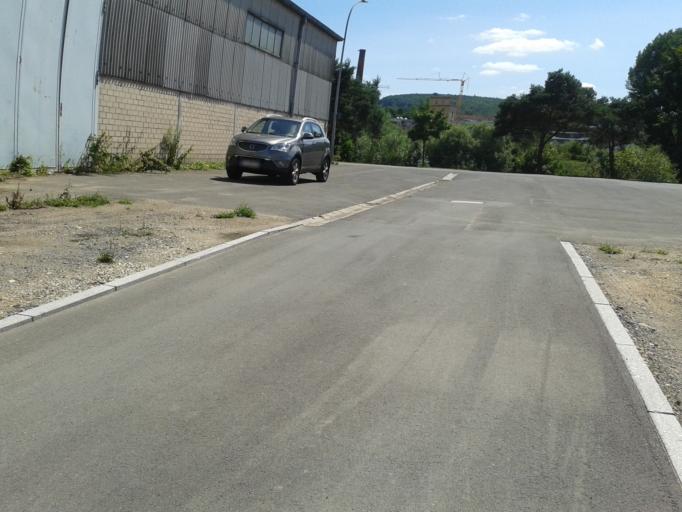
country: DE
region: Bavaria
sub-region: Upper Franconia
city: Hallstadt
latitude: 49.9067
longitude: 10.8694
